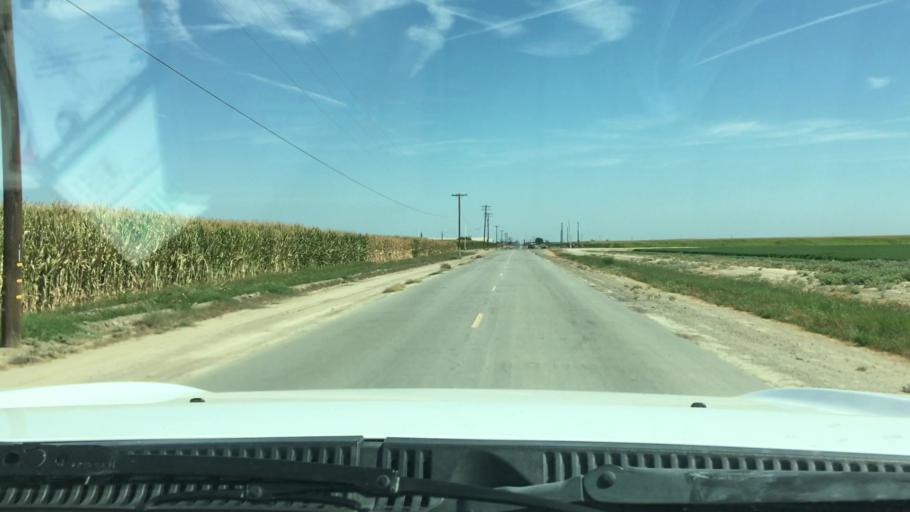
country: US
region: California
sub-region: Kern County
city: Buttonwillow
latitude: 35.4037
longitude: -119.3767
